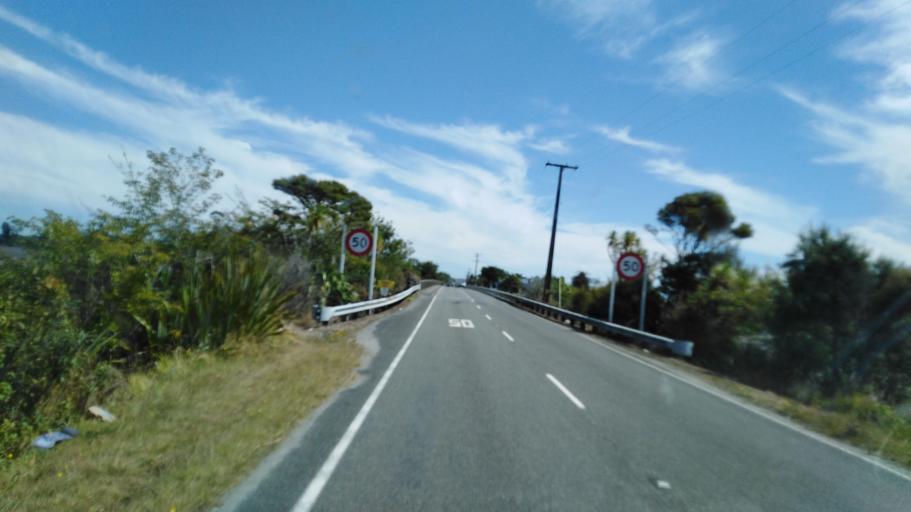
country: NZ
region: West Coast
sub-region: Buller District
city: Westport
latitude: -41.7518
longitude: 171.6267
